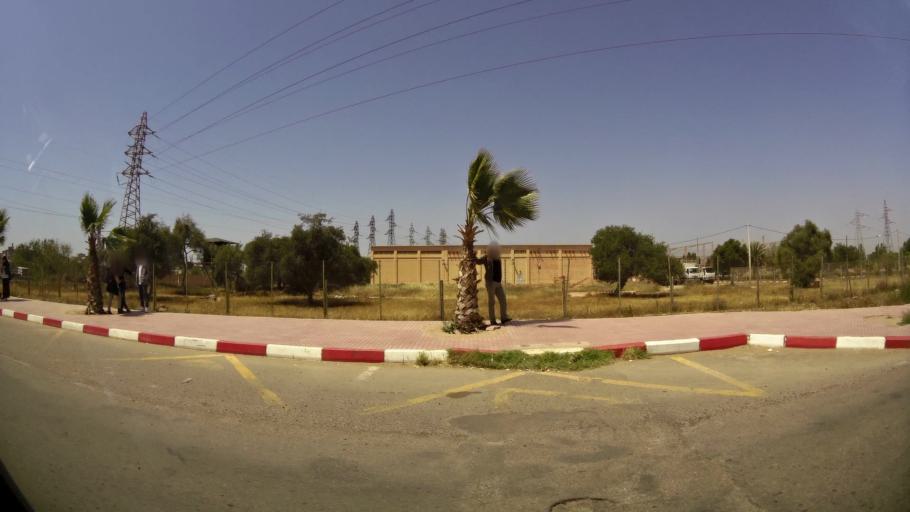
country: MA
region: Souss-Massa-Draa
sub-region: Inezgane-Ait Mellou
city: Inezgane
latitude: 30.3534
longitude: -9.4882
